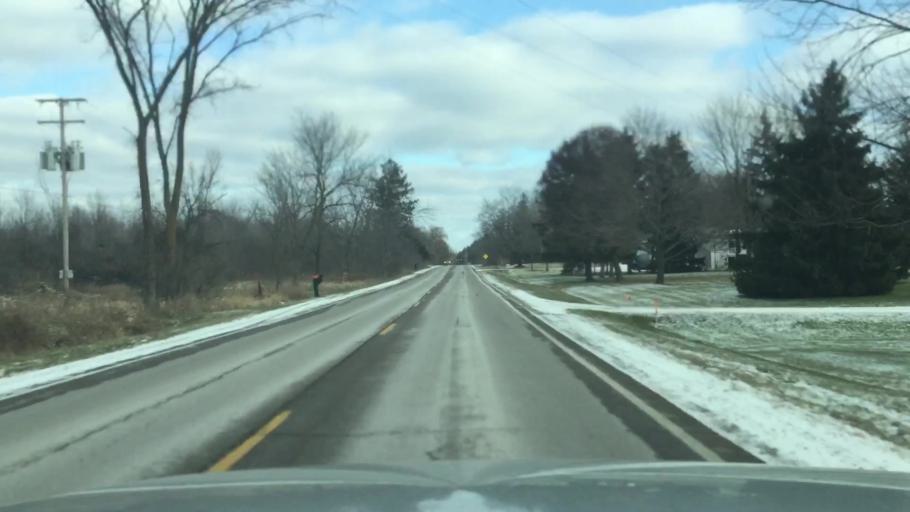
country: US
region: Michigan
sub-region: Genesee County
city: Linden
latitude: 42.8574
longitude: -83.7760
